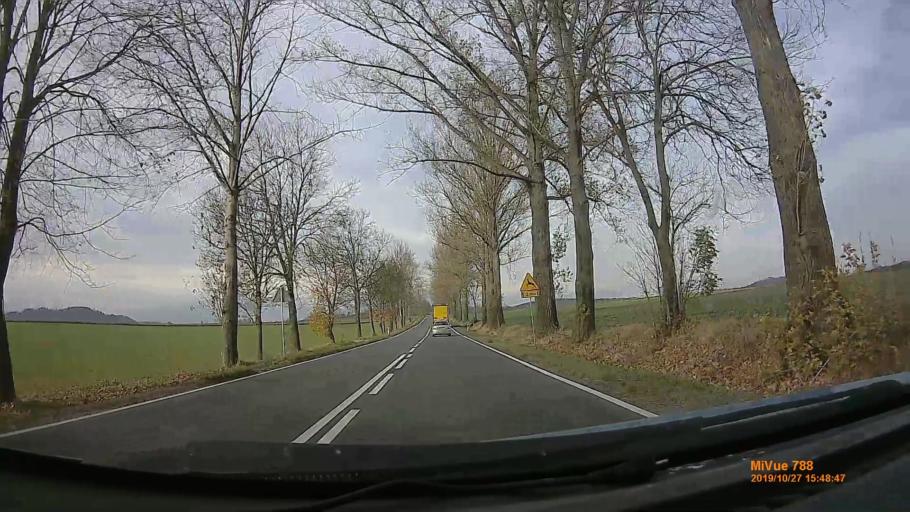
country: PL
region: Lower Silesian Voivodeship
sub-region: Powiat klodzki
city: Bozkow
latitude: 50.5005
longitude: 16.5849
